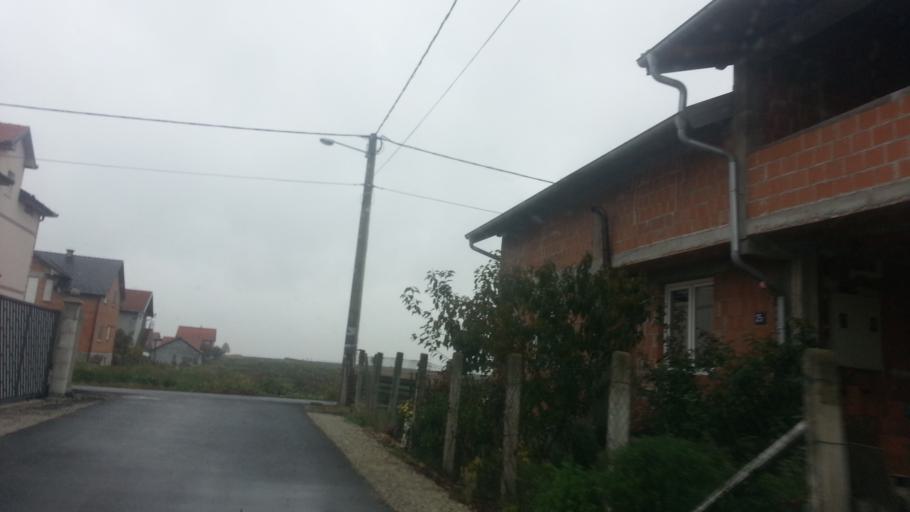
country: RS
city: Novi Banovci
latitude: 44.9056
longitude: 20.2971
